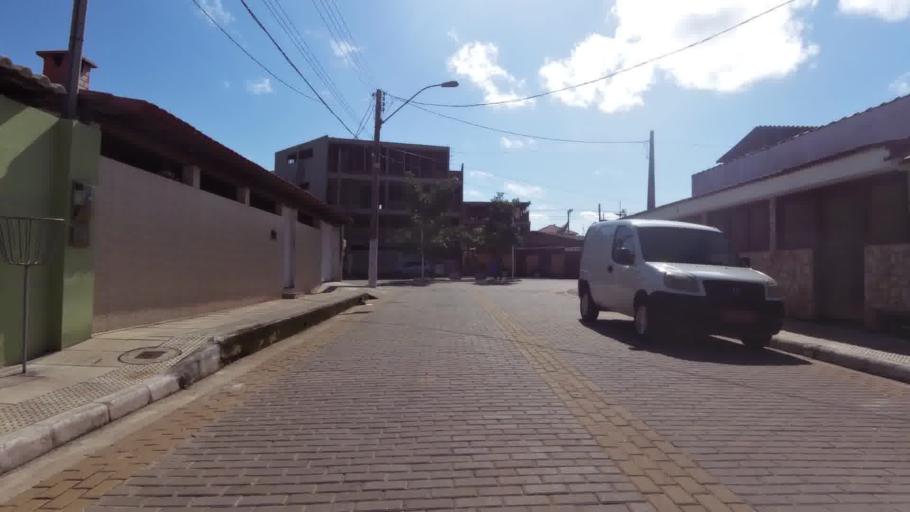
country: BR
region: Espirito Santo
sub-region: Piuma
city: Piuma
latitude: -20.8112
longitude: -40.6369
